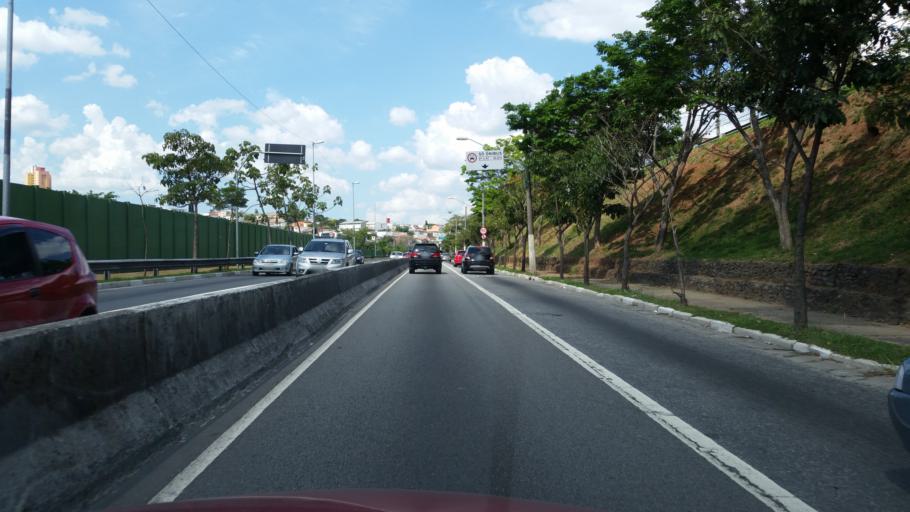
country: BR
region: Sao Paulo
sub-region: Guarulhos
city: Guarulhos
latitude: -23.5282
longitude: -46.5130
